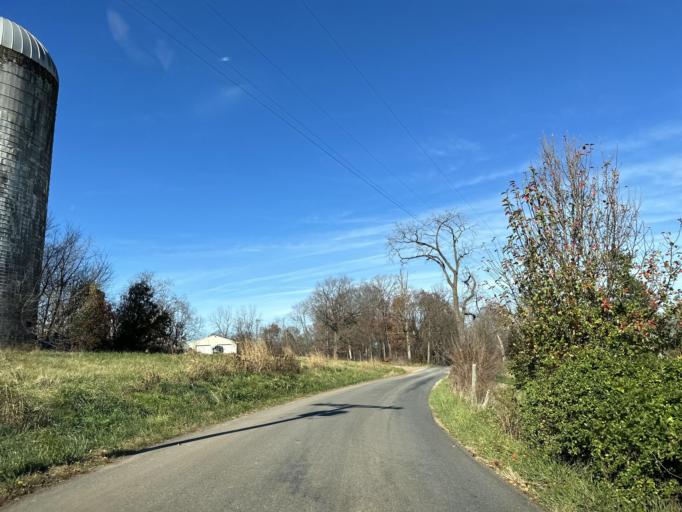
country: US
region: Virginia
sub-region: Augusta County
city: Weyers Cave
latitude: 38.2205
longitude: -78.9222
